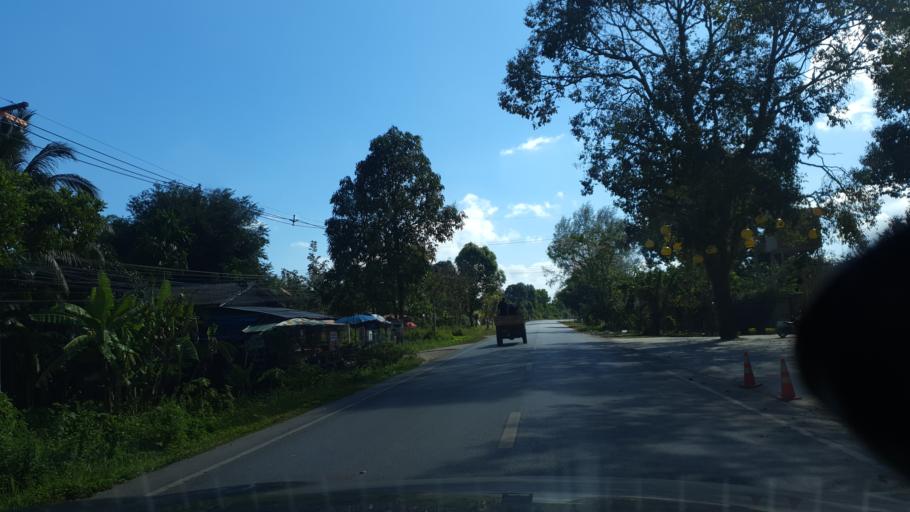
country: TH
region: Phangnga
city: Ban Ao Nang
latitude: 8.0296
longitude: 98.8670
